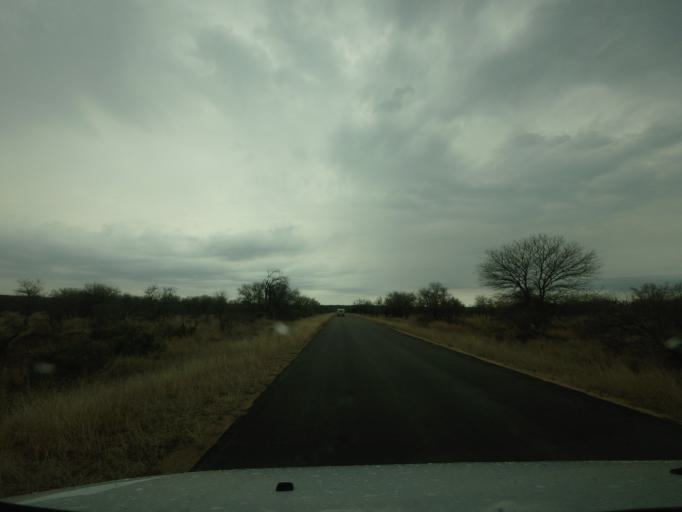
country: ZA
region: Limpopo
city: Thulamahashi
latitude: -24.4703
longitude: 31.4338
